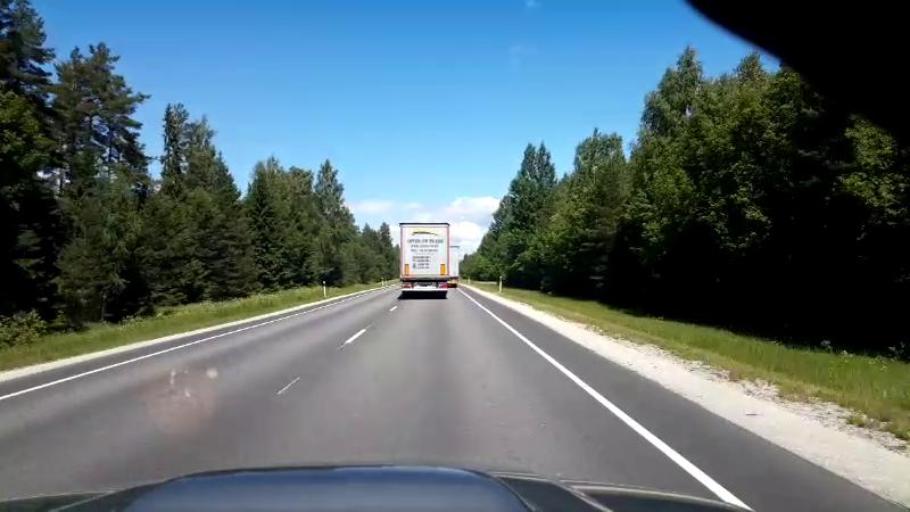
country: EE
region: Paernumaa
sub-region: Paernu linn
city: Parnu
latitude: 58.1102
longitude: 24.5093
